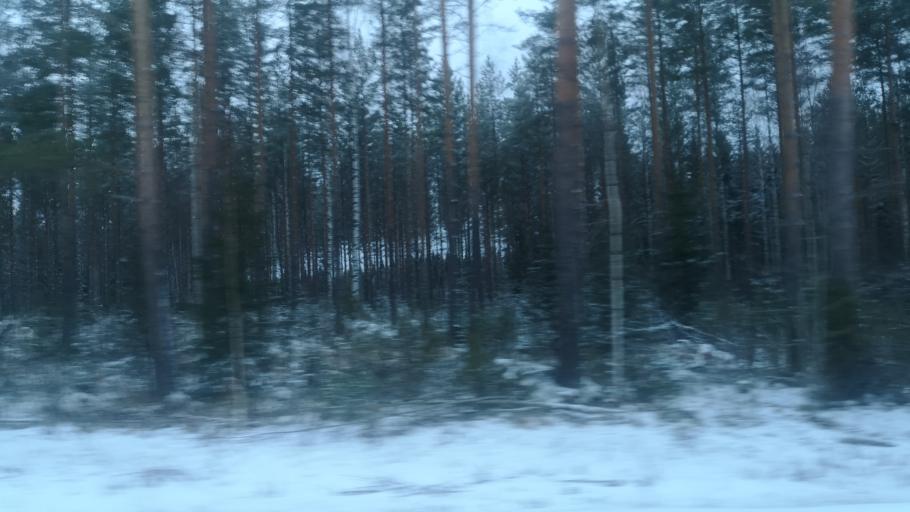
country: FI
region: Southern Savonia
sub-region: Savonlinna
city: Enonkoski
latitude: 62.1094
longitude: 28.6171
